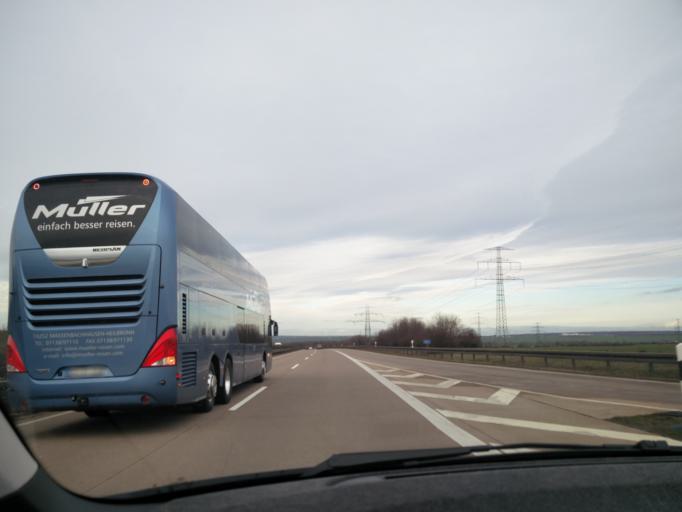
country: DE
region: Thuringia
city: Alkersleben
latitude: 50.8536
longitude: 11.0085
